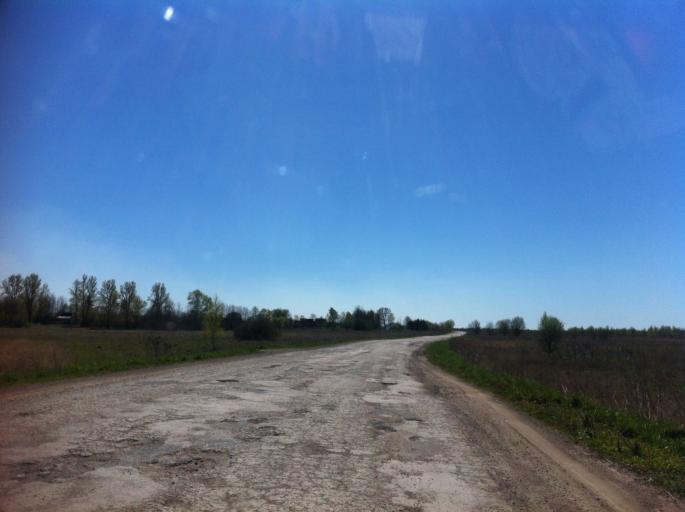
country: RU
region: Pskov
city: Izborsk
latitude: 57.7661
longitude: 27.9450
